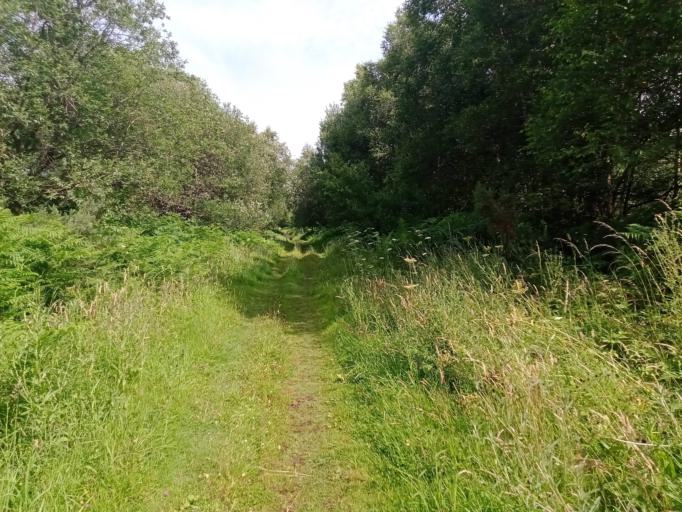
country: IE
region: Leinster
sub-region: Laois
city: Abbeyleix
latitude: 52.8926
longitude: -7.3502
